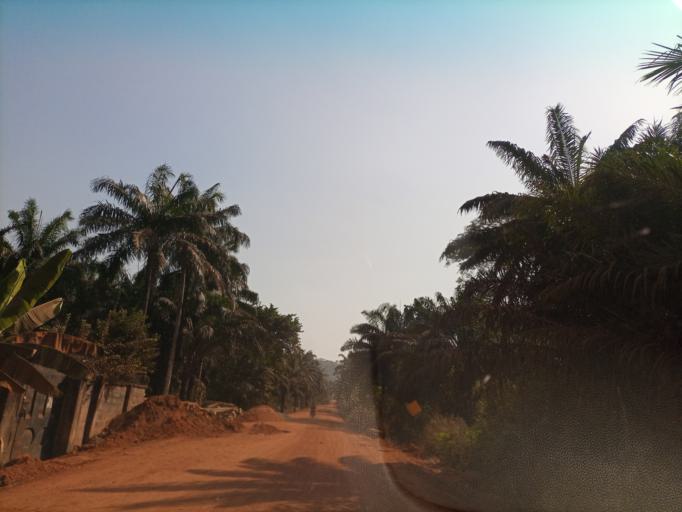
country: NG
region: Enugu
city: Aku
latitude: 6.7058
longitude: 7.3213
